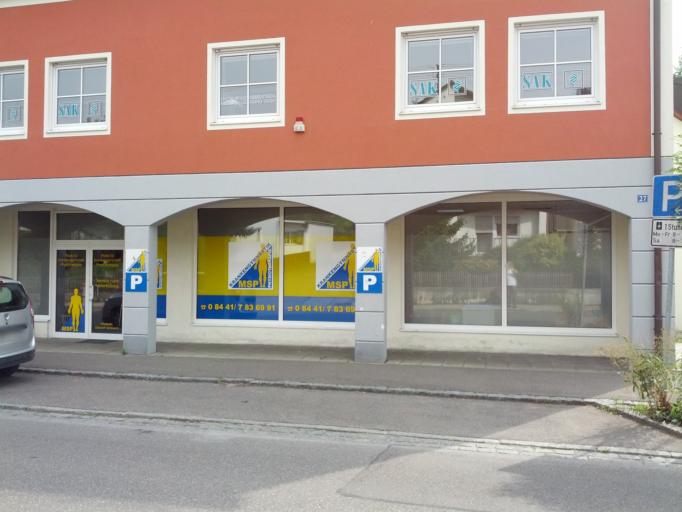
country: DE
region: Bavaria
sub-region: Upper Bavaria
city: Pfaffenhofen an der Ilm
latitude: 48.5305
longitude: 11.5005
